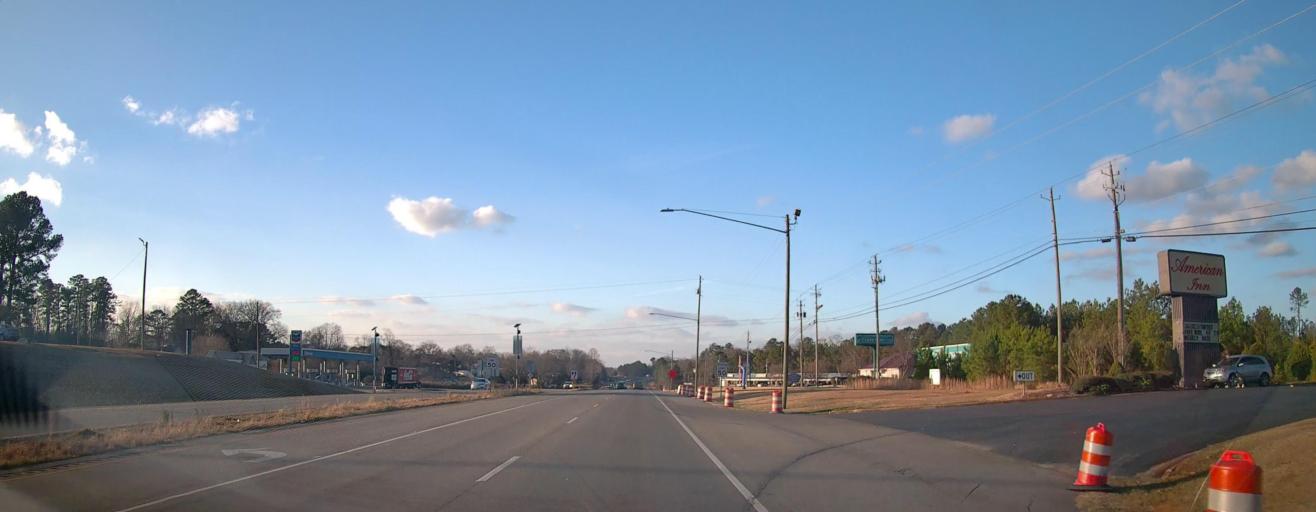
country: US
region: Alabama
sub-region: Calhoun County
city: Saks
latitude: 33.7036
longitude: -85.8320
